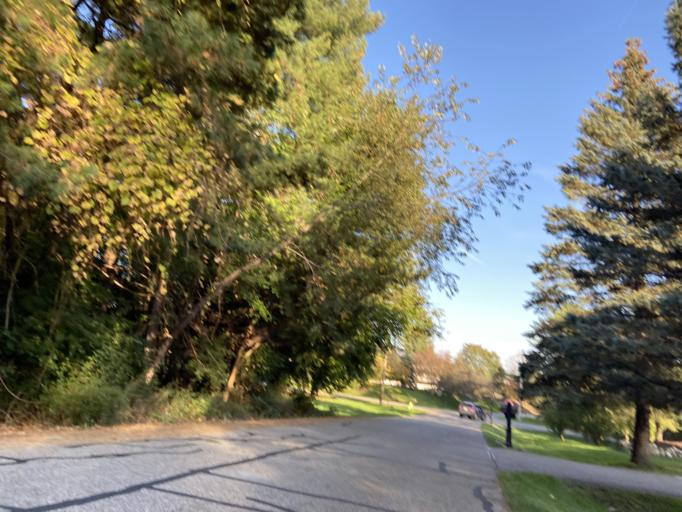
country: US
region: Michigan
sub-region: Oakland County
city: Franklin
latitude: 42.5110
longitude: -83.3311
